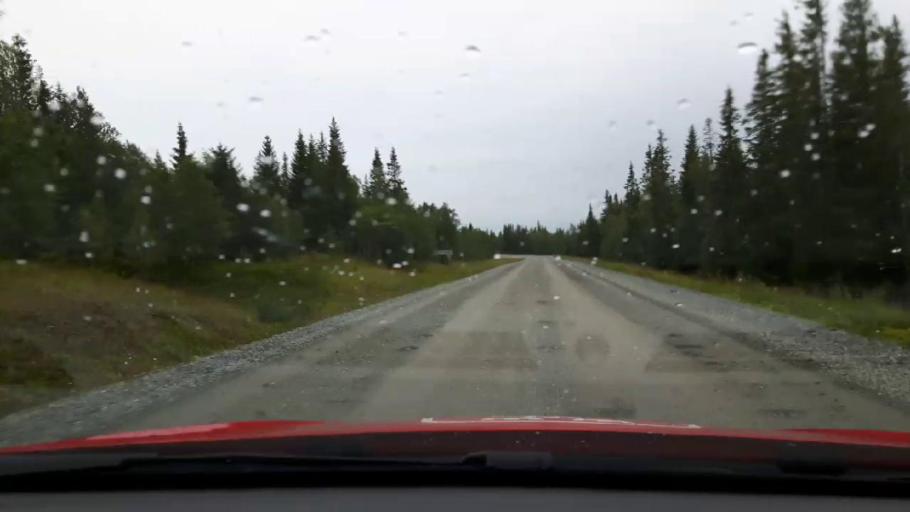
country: NO
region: Nord-Trondelag
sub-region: Meraker
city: Meraker
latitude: 63.5176
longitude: 12.4111
